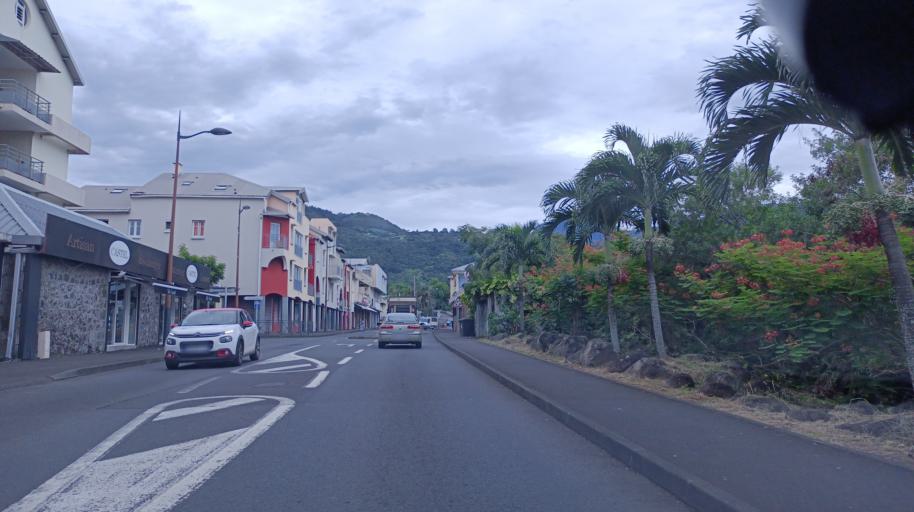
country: RE
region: Reunion
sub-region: Reunion
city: Saint-Joseph
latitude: -21.3777
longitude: 55.6153
